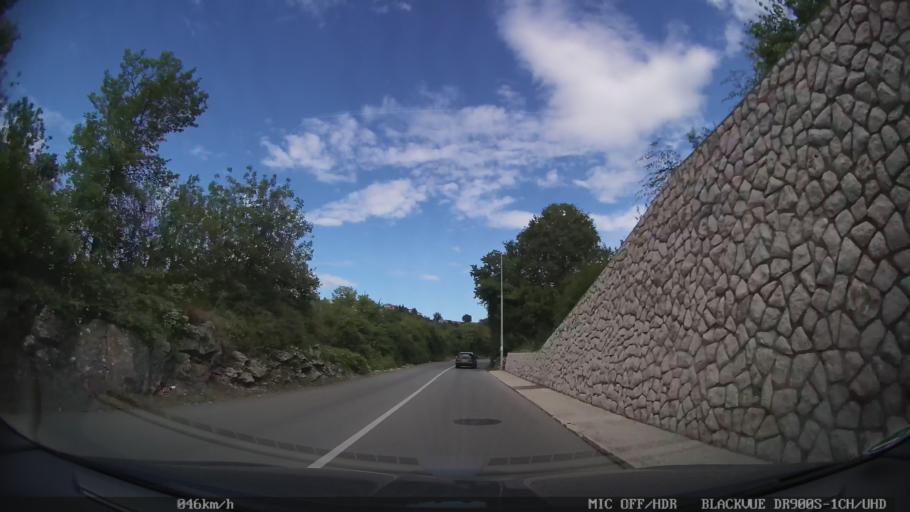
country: HR
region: Primorsko-Goranska
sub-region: Grad Krk
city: Krk
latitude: 45.0299
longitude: 14.5758
